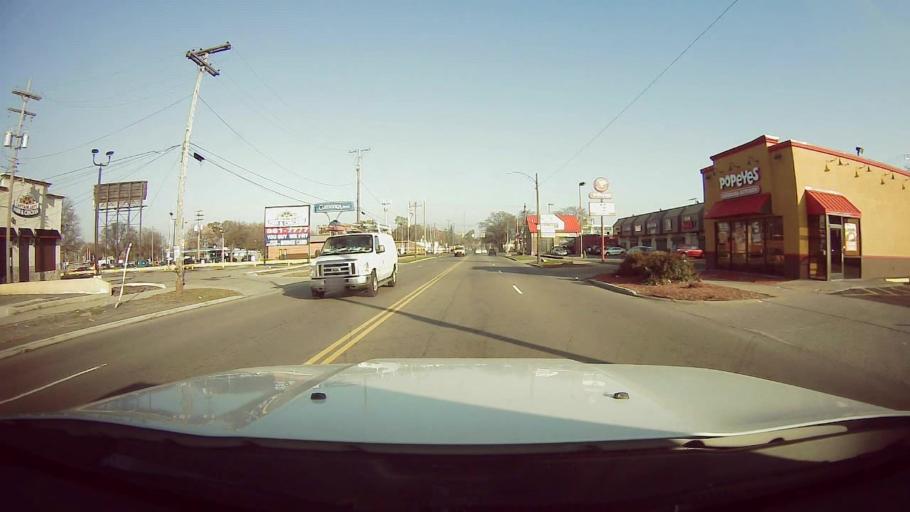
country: US
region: Michigan
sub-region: Oakland County
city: Oak Park
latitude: 42.4156
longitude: -83.1701
